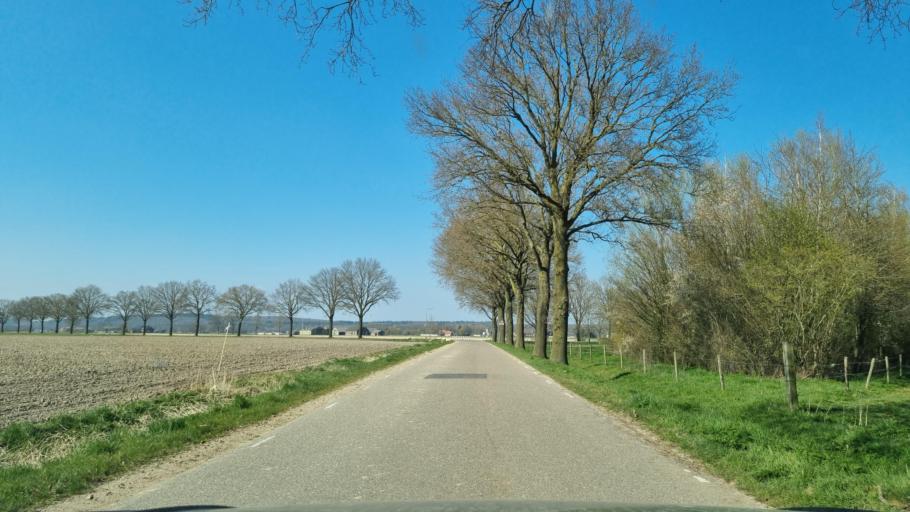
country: NL
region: Limburg
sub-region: Gemeente Gennep
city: Gennep
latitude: 51.7229
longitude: 5.9972
